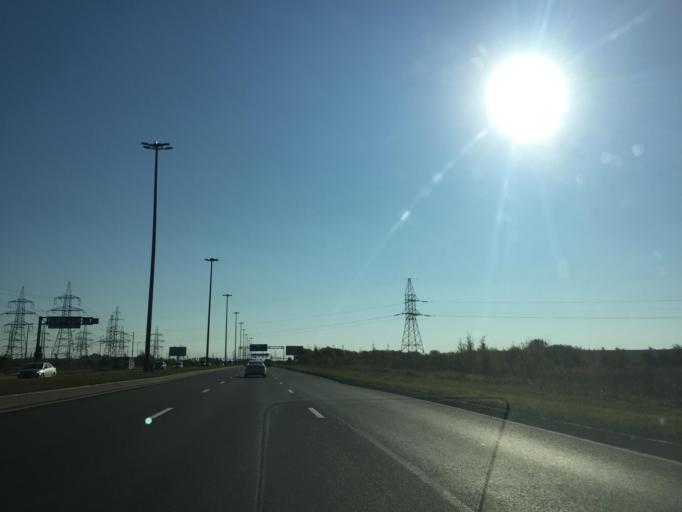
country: RU
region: St.-Petersburg
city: Petro-Slavyanka
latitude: 59.7535
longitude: 30.5230
